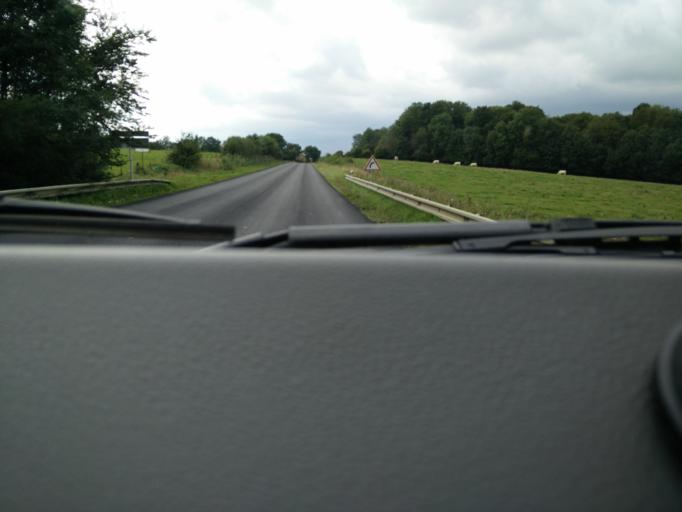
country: FR
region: Champagne-Ardenne
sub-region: Departement des Ardennes
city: Signy-le-Petit
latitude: 49.8712
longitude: 4.3519
